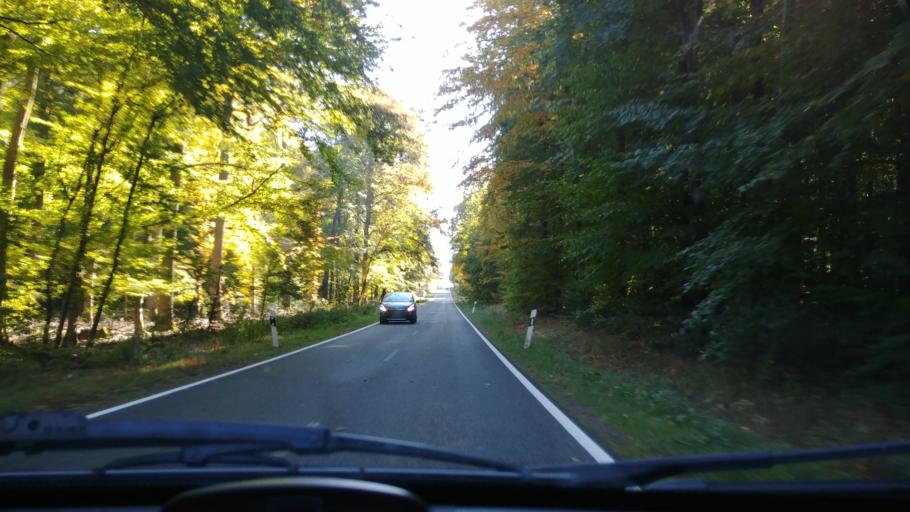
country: DE
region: Hesse
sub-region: Regierungsbezirk Darmstadt
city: Bad Schwalbach
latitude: 50.1722
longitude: 8.1031
